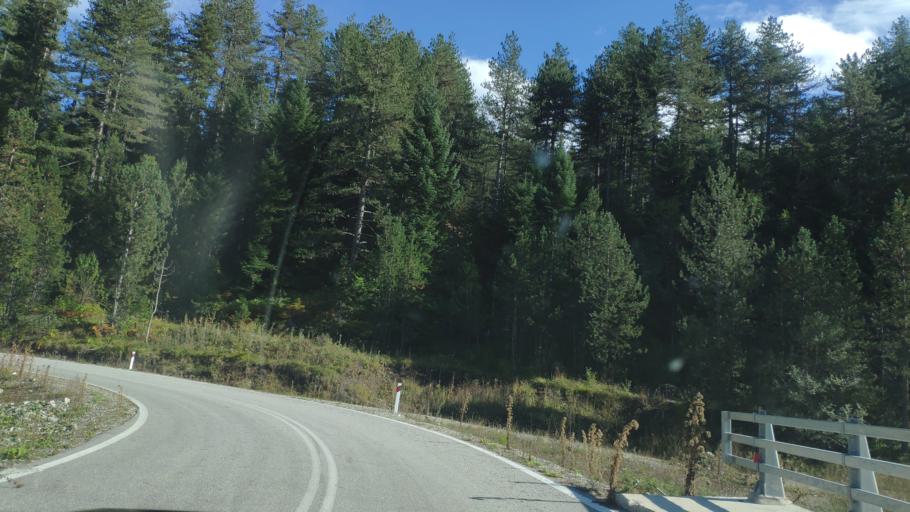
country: AL
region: Korce
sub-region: Rrethi i Devollit
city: Miras
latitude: 40.4094
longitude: 20.8742
